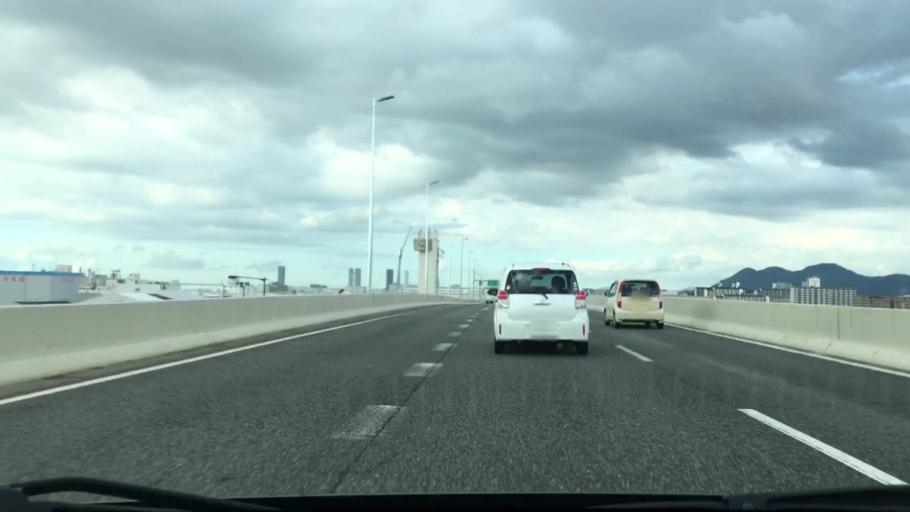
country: JP
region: Fukuoka
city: Fukuoka-shi
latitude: 33.6177
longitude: 130.4119
